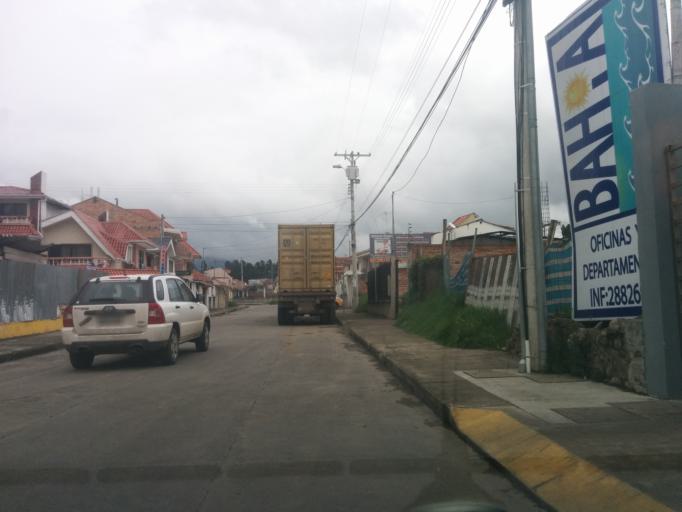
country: EC
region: Azuay
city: Cuenca
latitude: -2.9097
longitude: -79.0230
